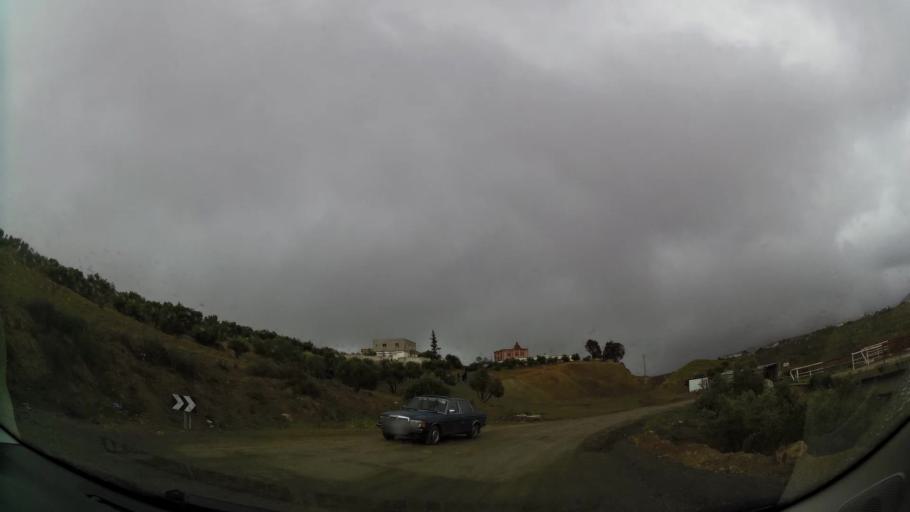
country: MA
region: Oriental
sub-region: Nador
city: Midar
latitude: 34.8909
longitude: -3.7592
